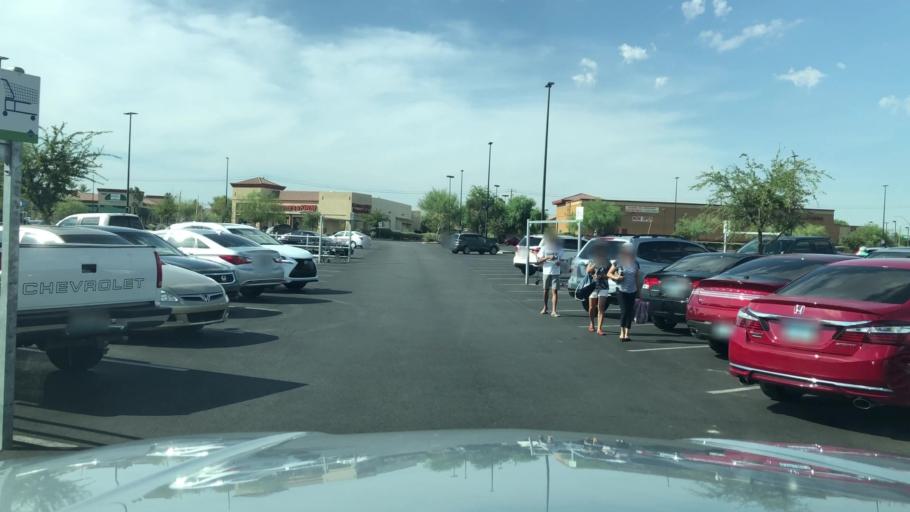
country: US
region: Nevada
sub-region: Clark County
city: Whitney
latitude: 36.0228
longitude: -115.1260
